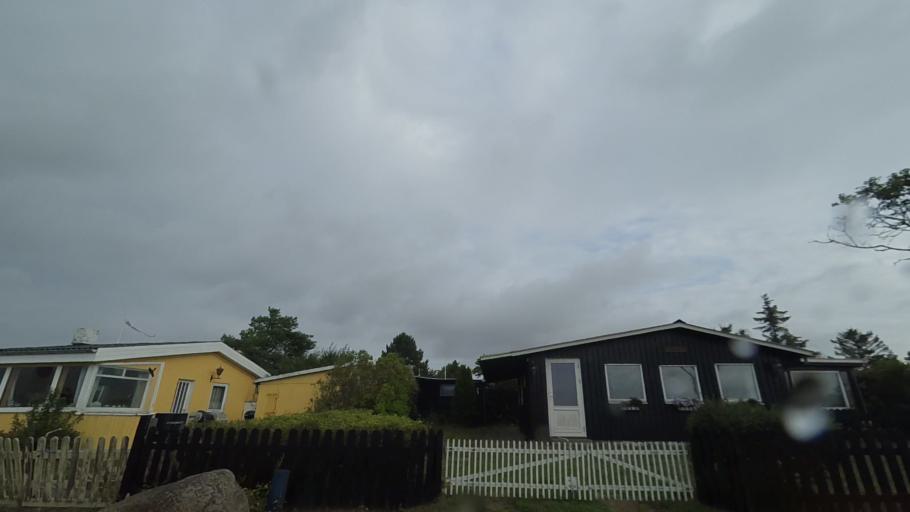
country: DK
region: Central Jutland
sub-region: Syddjurs Kommune
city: Ronde
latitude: 56.2959
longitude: 10.4321
